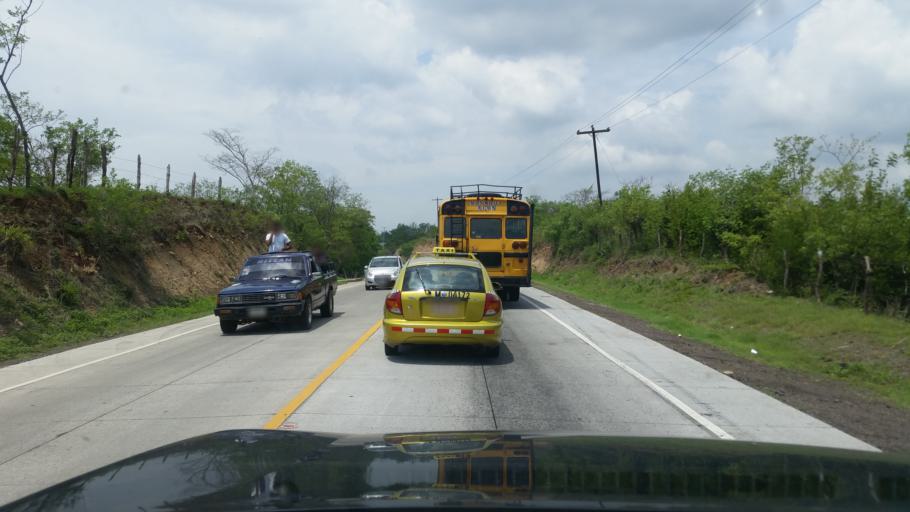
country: NI
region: Managua
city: Ciudad Sandino
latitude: 12.0816
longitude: -86.4116
